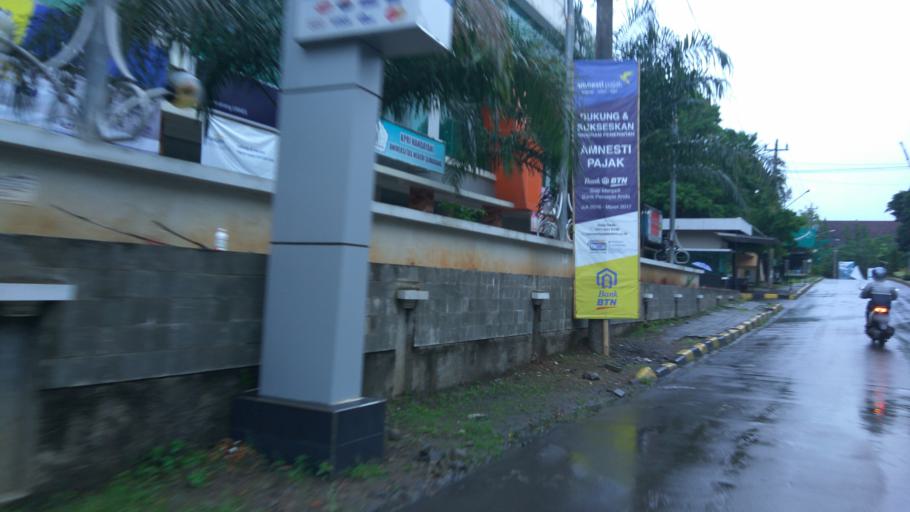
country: ID
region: Central Java
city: Semarang
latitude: -7.0488
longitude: 110.3957
